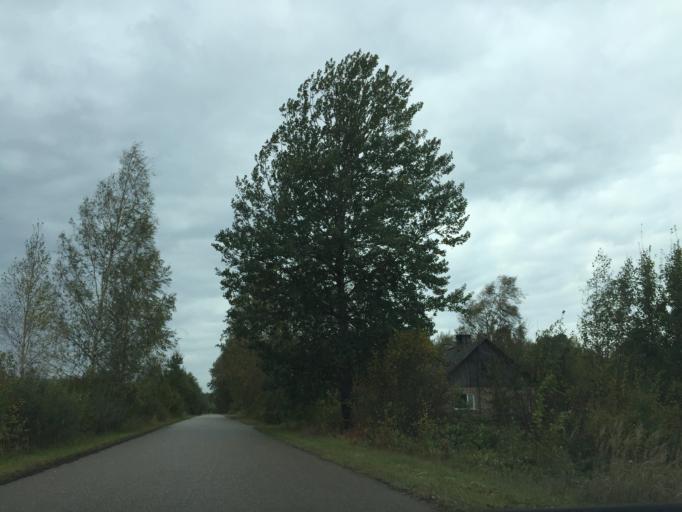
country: LV
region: Jelgava
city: Jelgava
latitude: 56.7495
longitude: 23.6958
